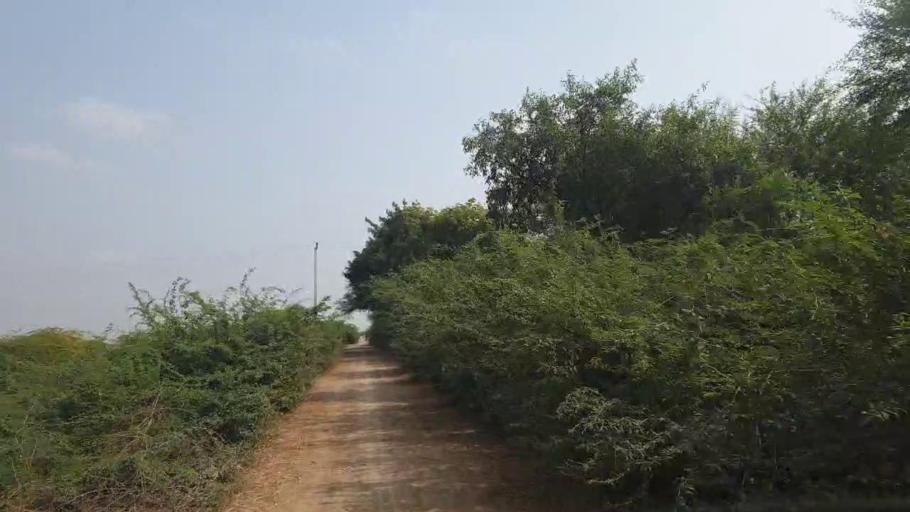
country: PK
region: Sindh
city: Badin
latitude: 24.5475
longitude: 68.7142
